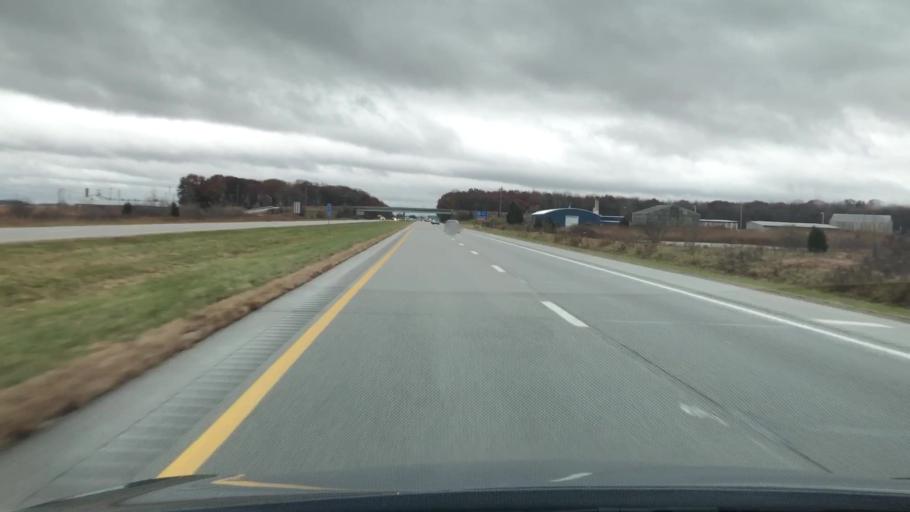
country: US
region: Ohio
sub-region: Wood County
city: Walbridge
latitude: 41.5763
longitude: -83.4714
